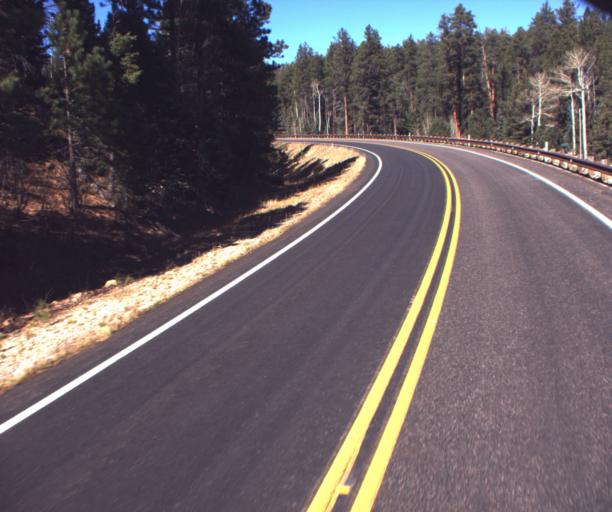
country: US
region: Arizona
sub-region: Coconino County
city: Grand Canyon
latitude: 36.5112
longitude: -112.1367
